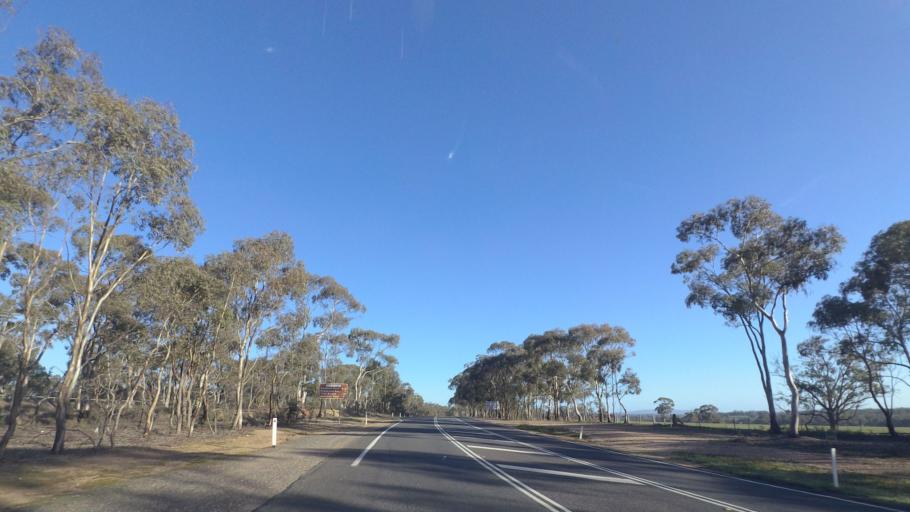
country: AU
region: Victoria
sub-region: Greater Bendigo
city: Kennington
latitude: -36.8550
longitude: 144.5068
